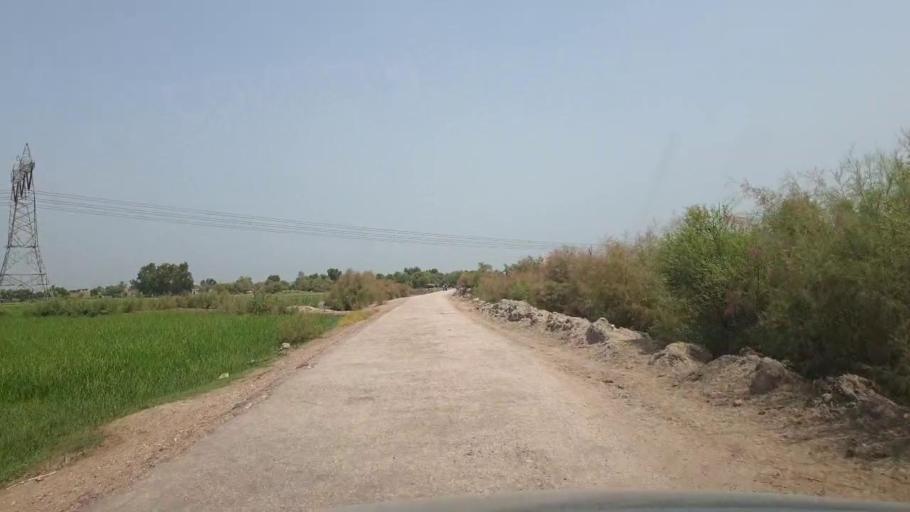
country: PK
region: Sindh
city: Madeji
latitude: 27.8045
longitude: 68.5202
